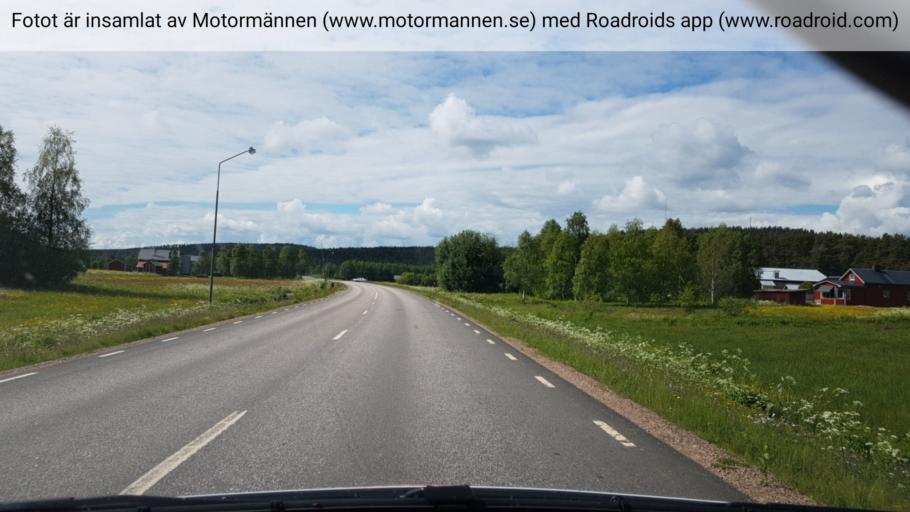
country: SE
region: Norrbotten
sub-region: Overtornea Kommun
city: OEvertornea
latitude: 66.4640
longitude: 23.6428
